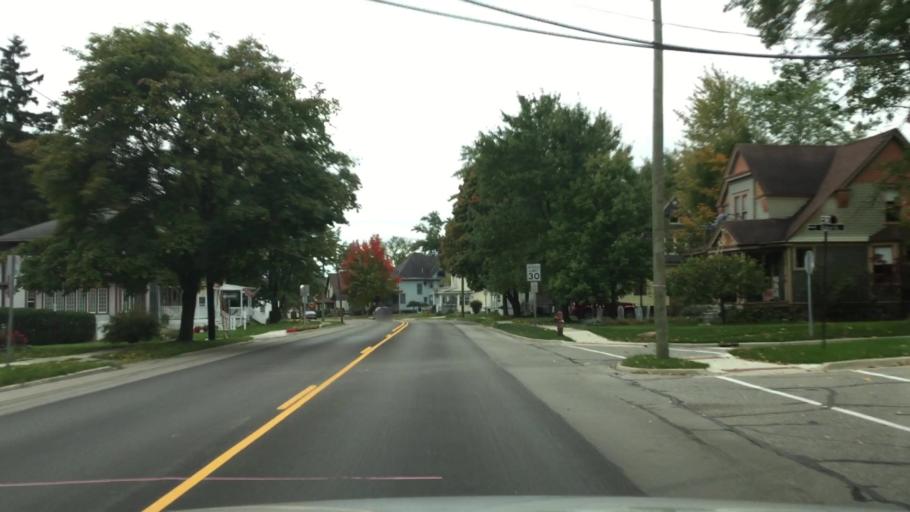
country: US
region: Michigan
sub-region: Macomb County
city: Richmond
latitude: 42.8156
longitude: -82.7595
